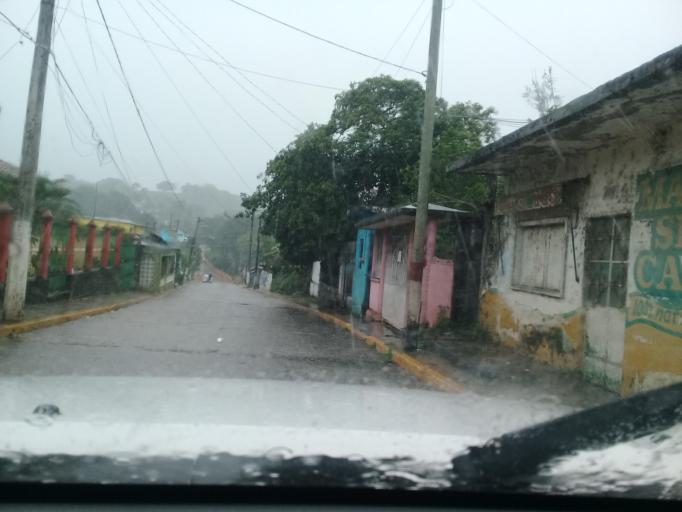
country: MX
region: Veracruz
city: Santiago Tuxtla
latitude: 18.4686
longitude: -95.3032
